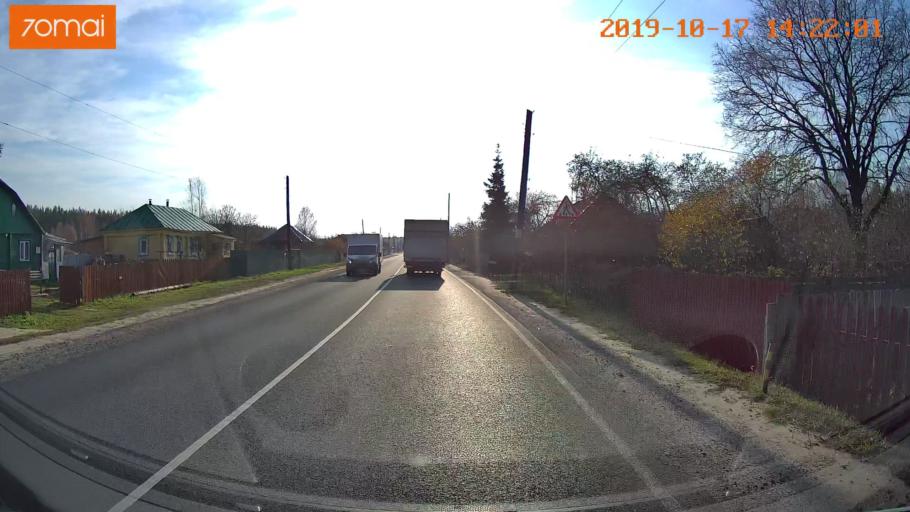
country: RU
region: Moskovskaya
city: Radovitskiy
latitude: 55.0334
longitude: 39.9717
